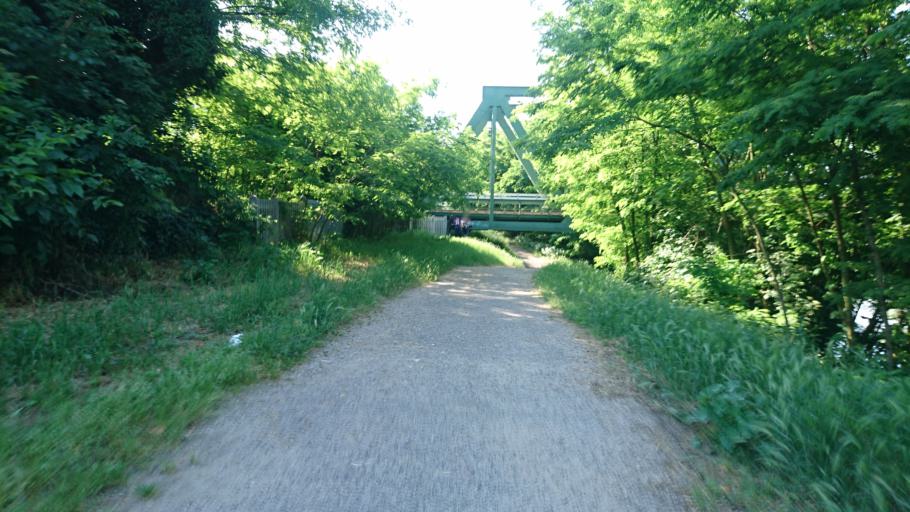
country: IT
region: Veneto
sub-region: Provincia di Verona
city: Boschi Sant'Anna
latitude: 45.1915
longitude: 11.3174
